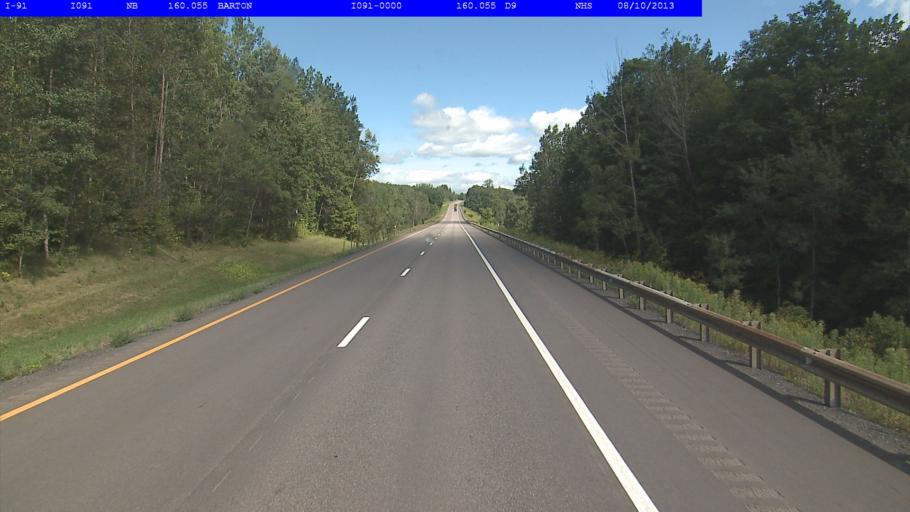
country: US
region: Vermont
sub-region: Orleans County
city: Newport
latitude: 44.7872
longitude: -72.2153
